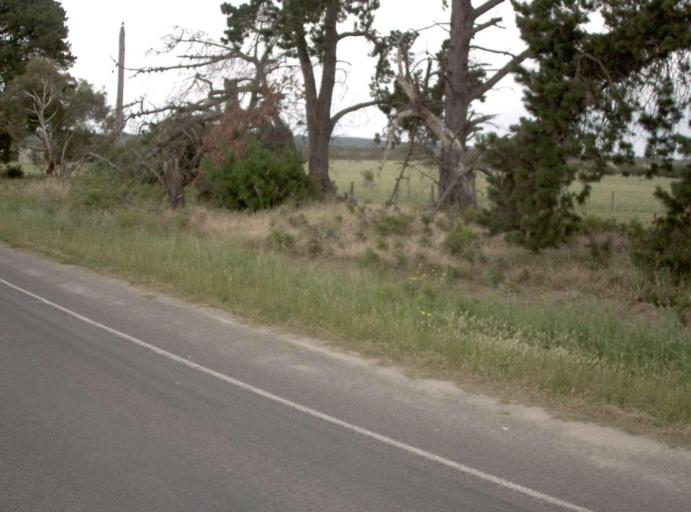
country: AU
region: Victoria
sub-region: Cardinia
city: Koo-Wee-Rup
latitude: -38.3233
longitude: 145.5872
